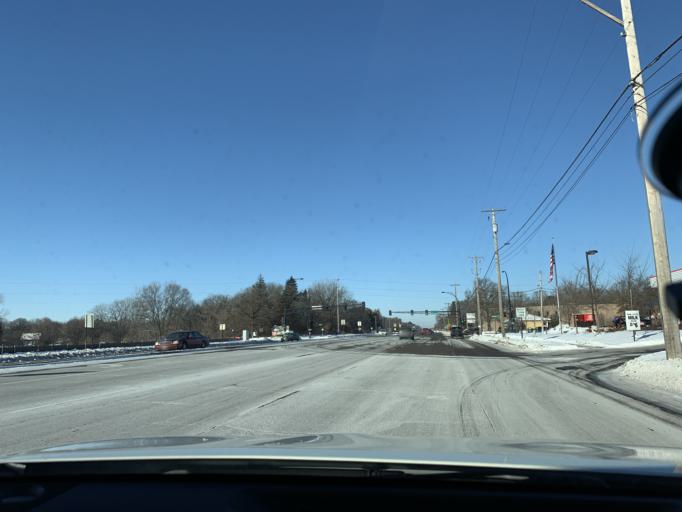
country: US
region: Minnesota
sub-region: Anoka County
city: Coon Rapids
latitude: 45.1542
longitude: -93.3051
